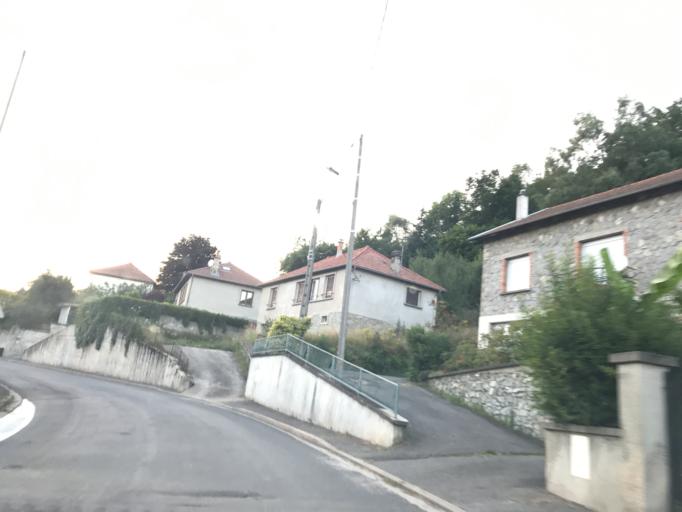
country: FR
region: Auvergne
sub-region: Departement du Puy-de-Dome
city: La Monnerie-le-Montel
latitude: 45.8729
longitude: 3.6015
